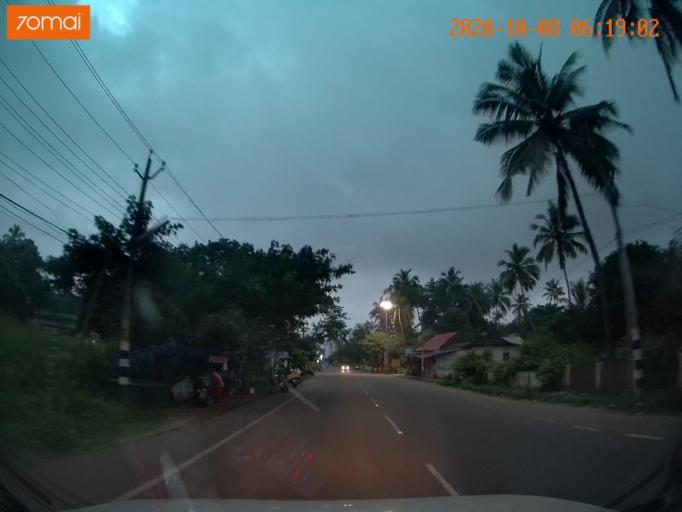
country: IN
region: Kerala
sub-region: Thrissur District
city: Trichur
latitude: 10.5156
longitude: 76.2413
